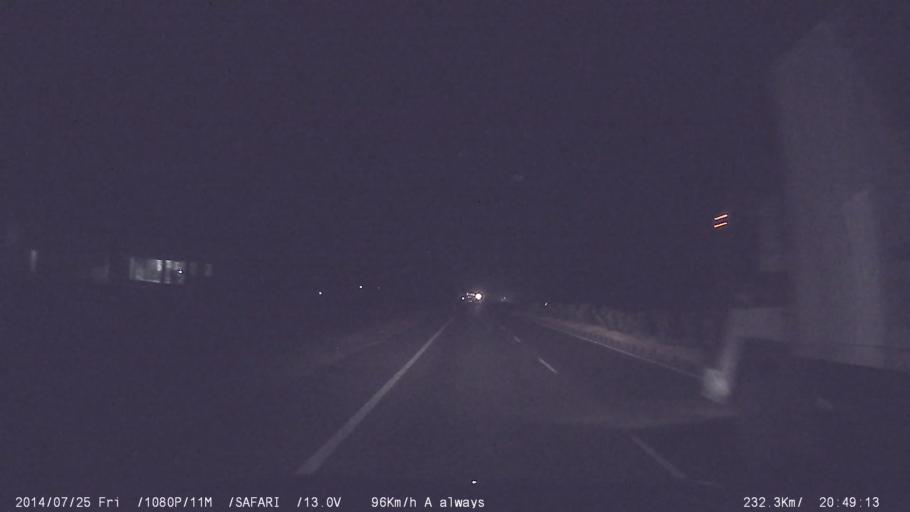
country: IN
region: Tamil Nadu
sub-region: Salem
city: Idappadi
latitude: 11.4933
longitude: 77.8652
